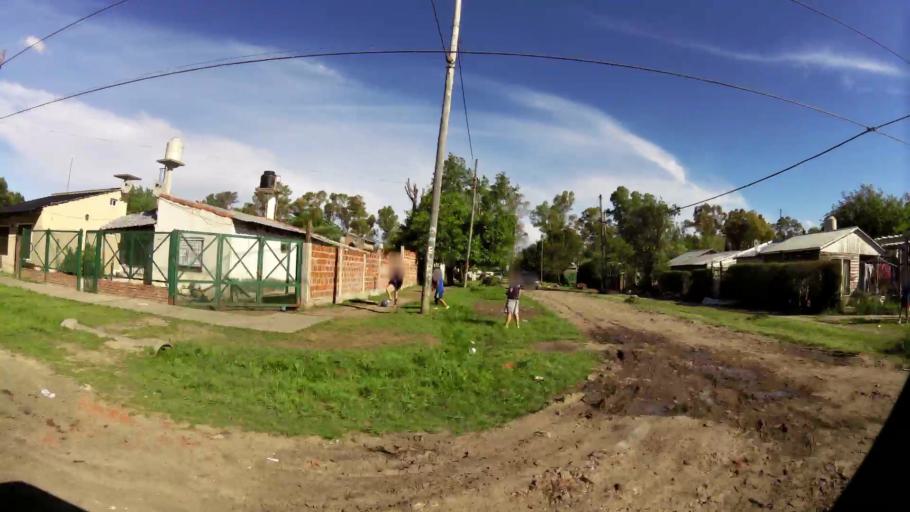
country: AR
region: Buenos Aires
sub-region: Partido de Almirante Brown
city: Adrogue
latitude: -34.8256
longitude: -58.3466
